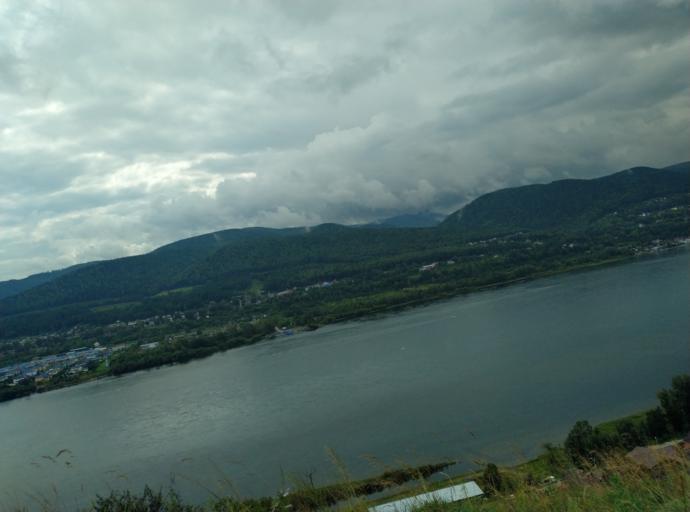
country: RU
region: Krasnoyarskiy
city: Krasnoyarsk
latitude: 55.9829
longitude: 92.7533
